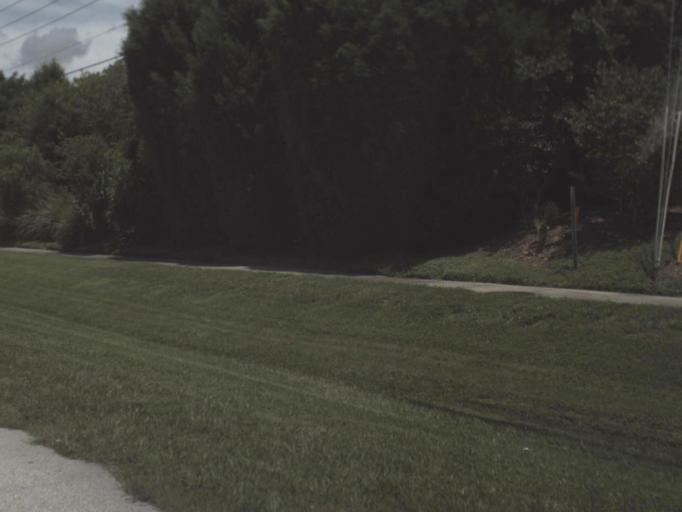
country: US
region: Florida
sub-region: Pinellas County
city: East Lake
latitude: 28.1277
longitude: -82.6969
